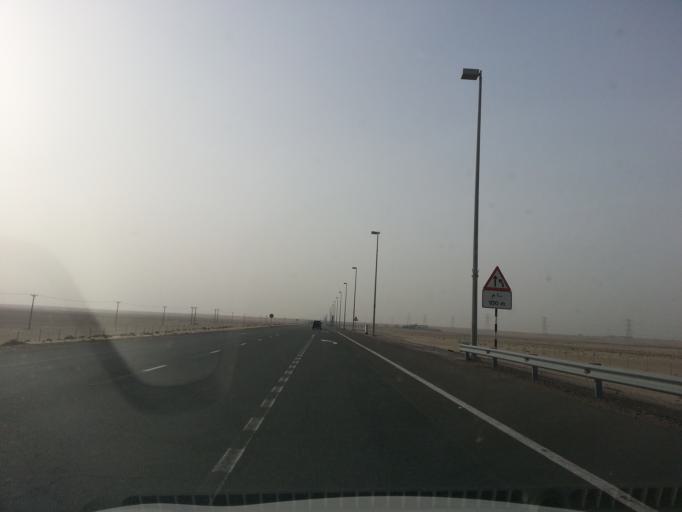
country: AE
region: Dubai
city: Dubai
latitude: 24.7957
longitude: 55.0746
